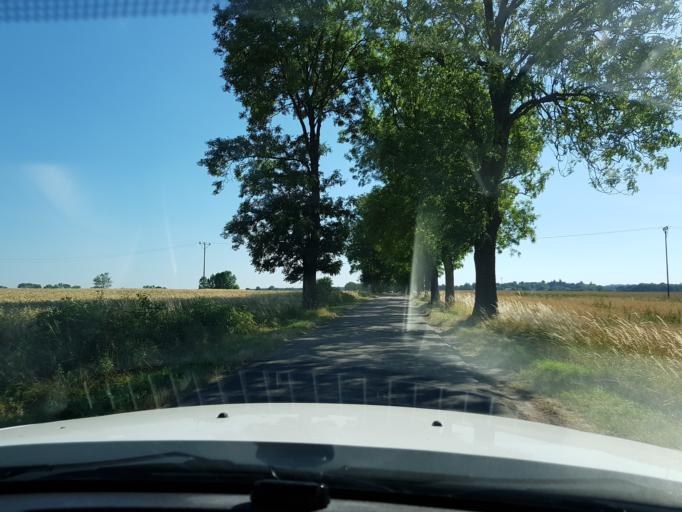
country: PL
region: West Pomeranian Voivodeship
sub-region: Powiat swidwinski
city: Slawoborze
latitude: 53.8296
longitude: 15.6940
